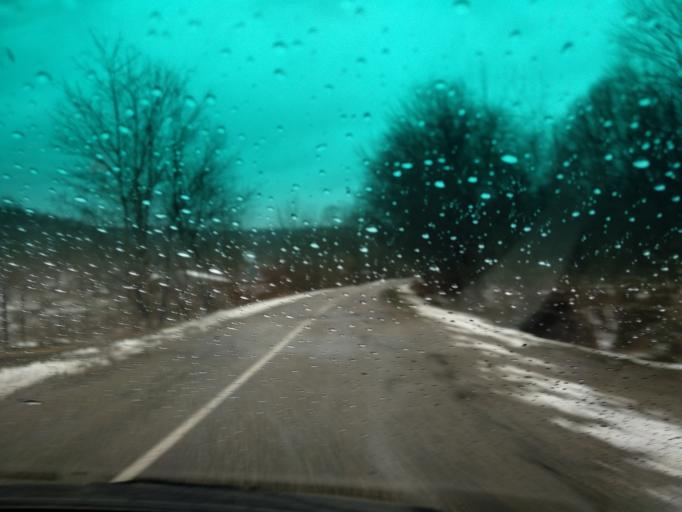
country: RU
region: Krasnodarskiy
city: Khadyzhensk
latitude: 44.2192
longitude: 39.3975
